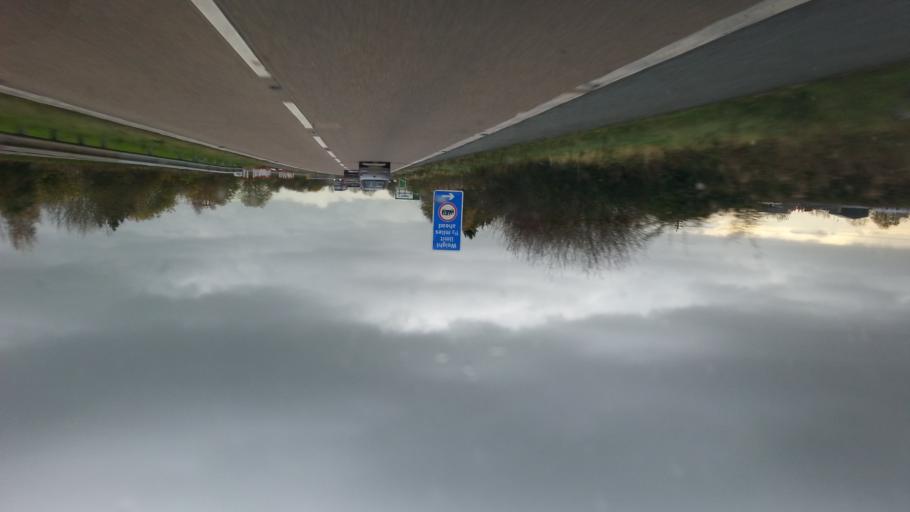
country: GB
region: England
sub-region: Leicestershire
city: Grimston
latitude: 52.8236
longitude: -1.0370
